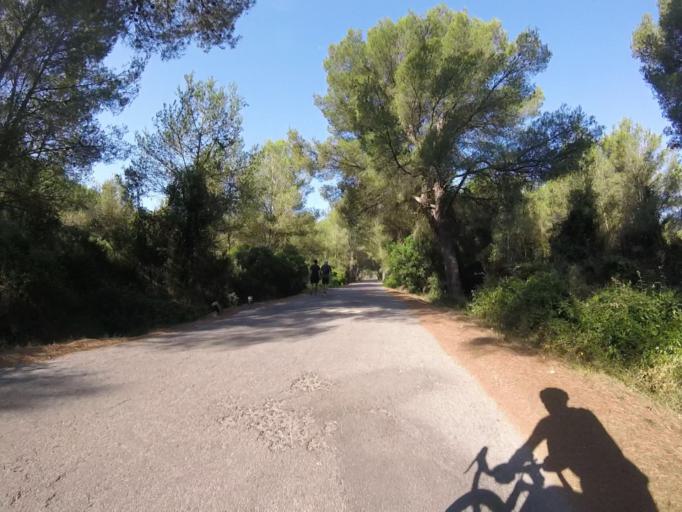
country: ES
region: Valencia
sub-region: Provincia de Castello
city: Benicassim
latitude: 40.0779
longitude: 0.0492
